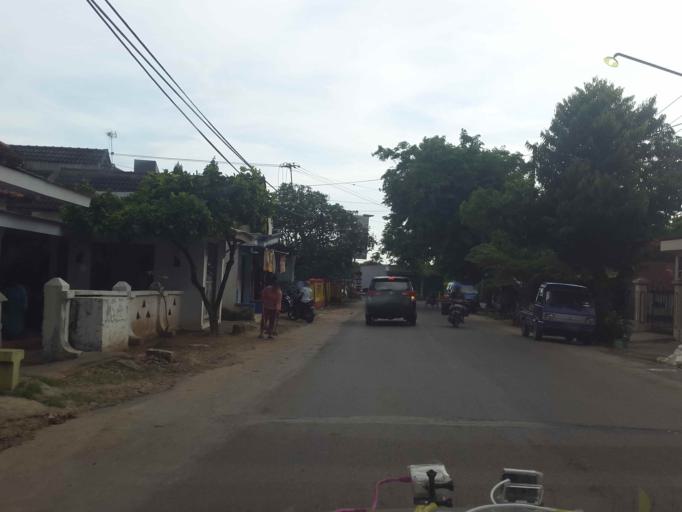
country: ID
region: East Java
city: Padusan
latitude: -6.9994
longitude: 113.8655
